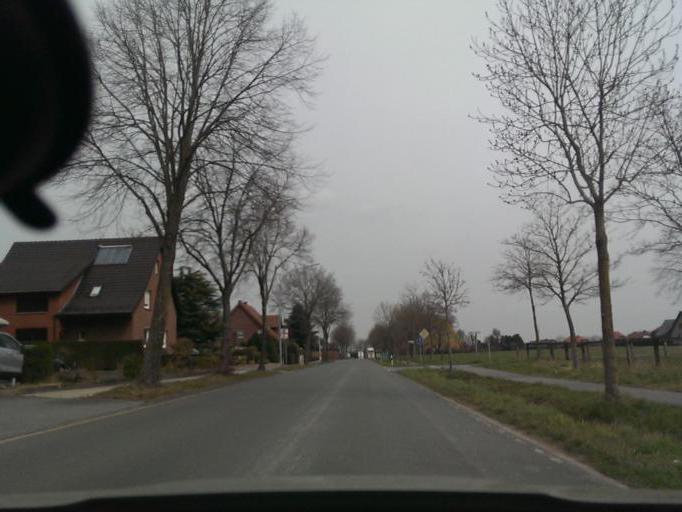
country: DE
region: North Rhine-Westphalia
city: Rietberg
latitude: 51.7511
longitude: 8.4629
